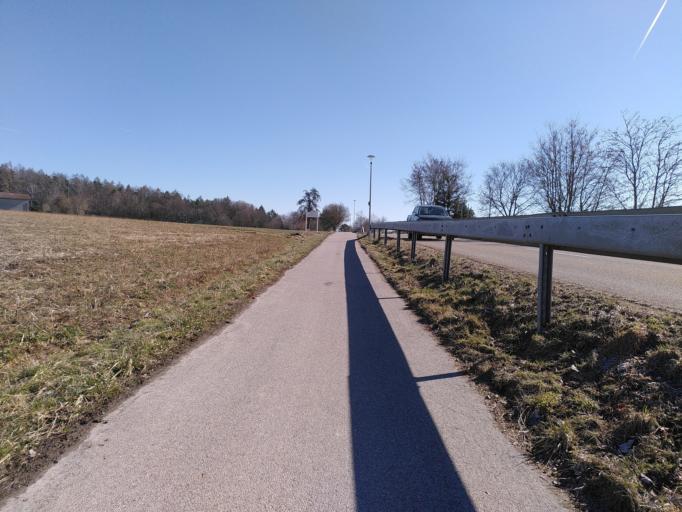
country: DE
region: Bavaria
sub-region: Upper Palatinate
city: Nittendorf
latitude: 49.0040
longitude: 11.9854
